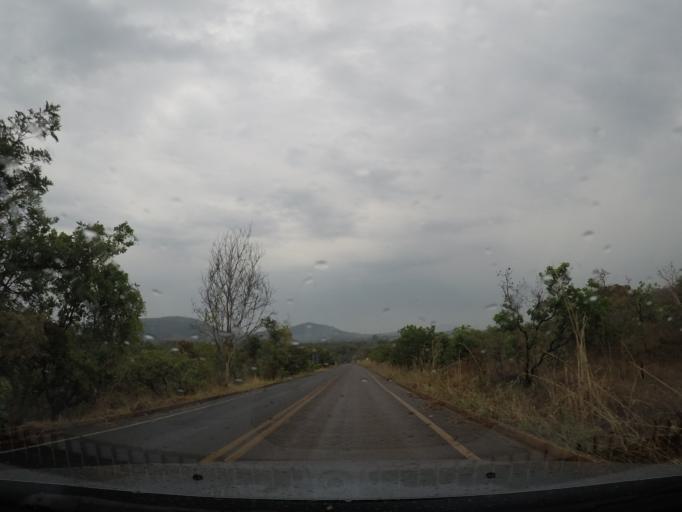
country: BR
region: Goias
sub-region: Pirenopolis
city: Pirenopolis
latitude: -15.8442
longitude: -48.9181
